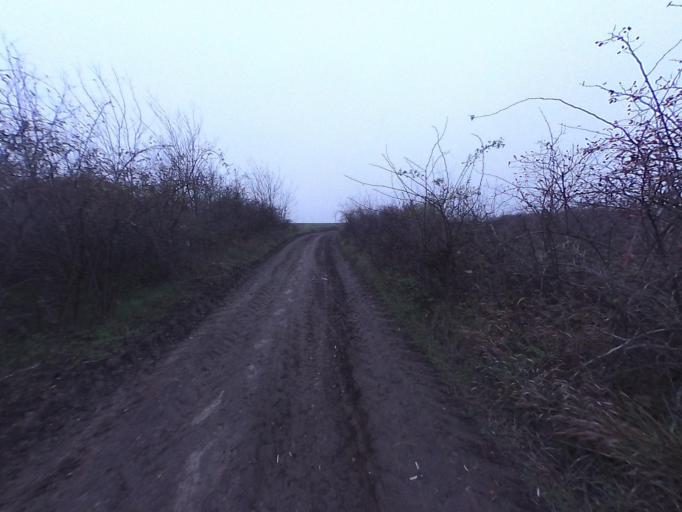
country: RO
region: Galati
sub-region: Comuna Balabanesti
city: Balabanesti
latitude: 46.1456
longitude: 27.7370
